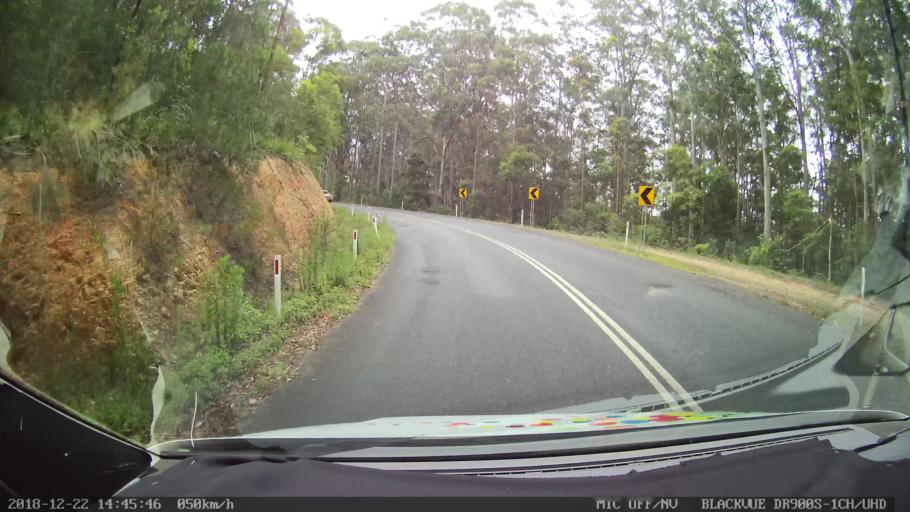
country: AU
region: New South Wales
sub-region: Bellingen
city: Dorrigo
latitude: -30.1711
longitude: 152.5665
